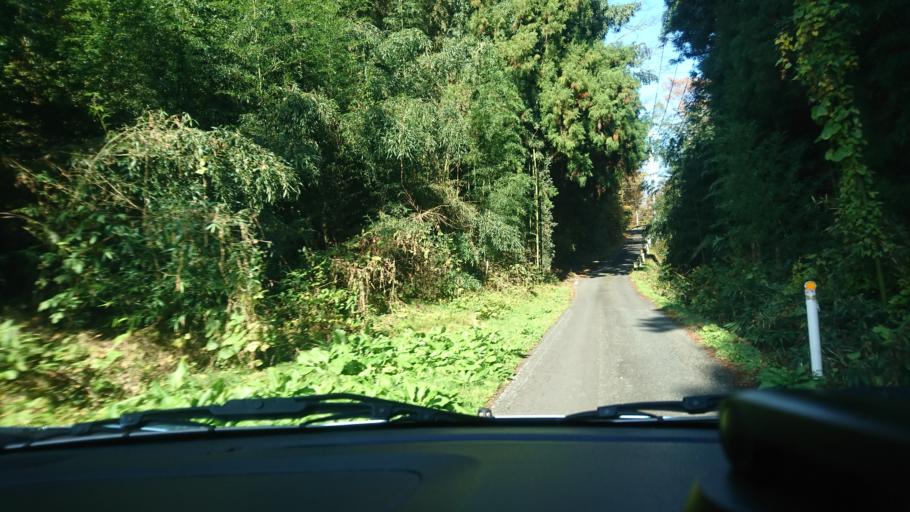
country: JP
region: Iwate
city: Ichinoseki
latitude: 38.7976
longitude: 141.2463
